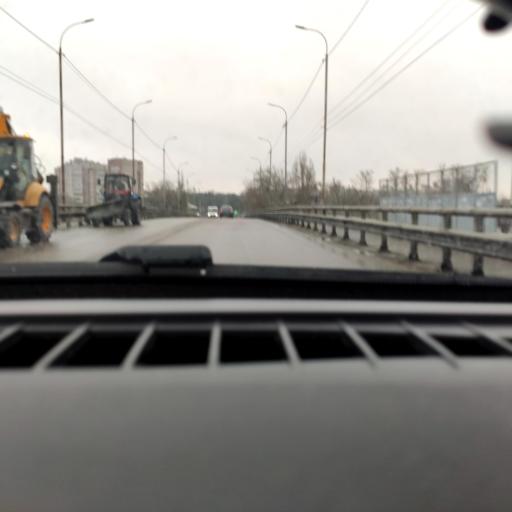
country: RU
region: Voronezj
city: Voronezh
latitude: 51.7266
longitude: 39.2610
